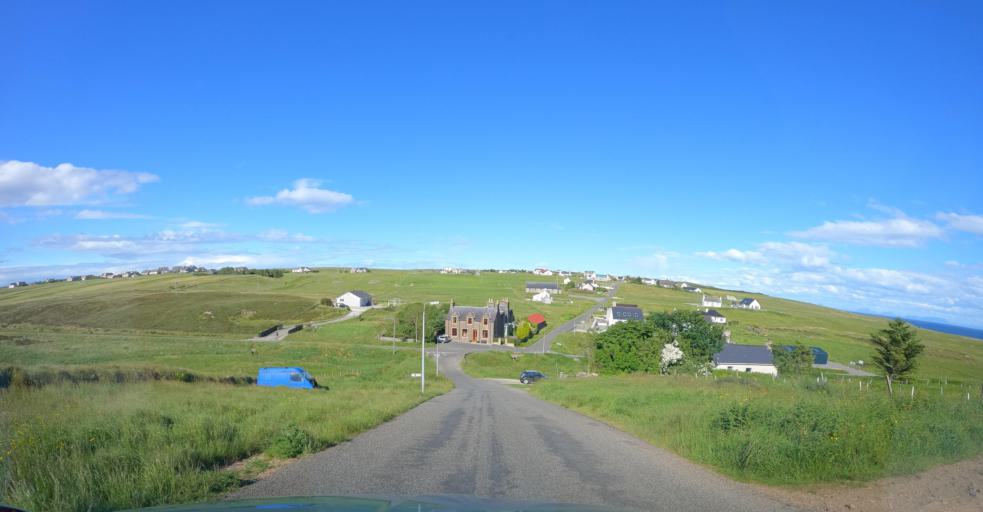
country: GB
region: Scotland
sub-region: Eilean Siar
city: Stornoway
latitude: 58.2036
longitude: -6.2161
